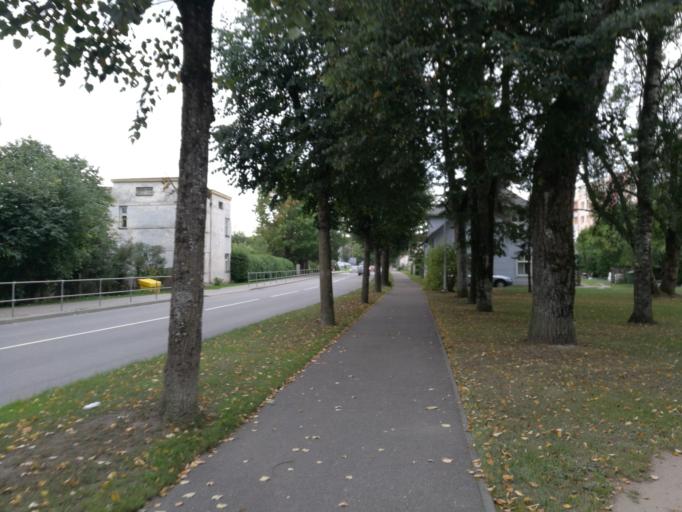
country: LV
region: Limbazu Rajons
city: Limbazi
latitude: 57.5101
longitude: 24.7142
